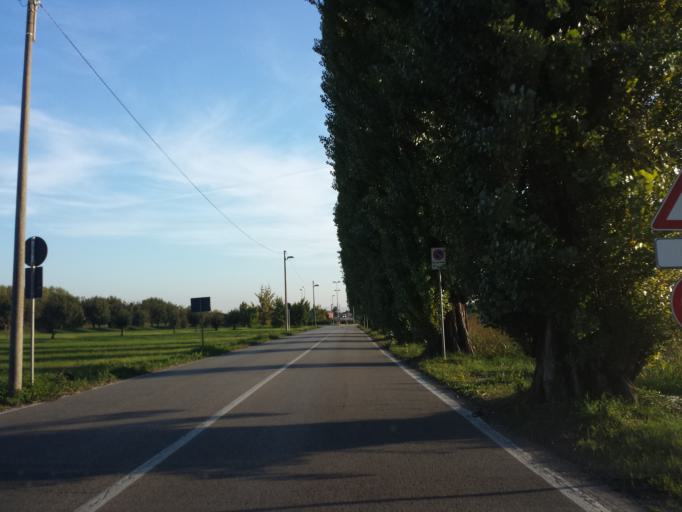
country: IT
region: Veneto
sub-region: Provincia di Vicenza
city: Crispi Cavour
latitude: 45.5850
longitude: 11.5333
